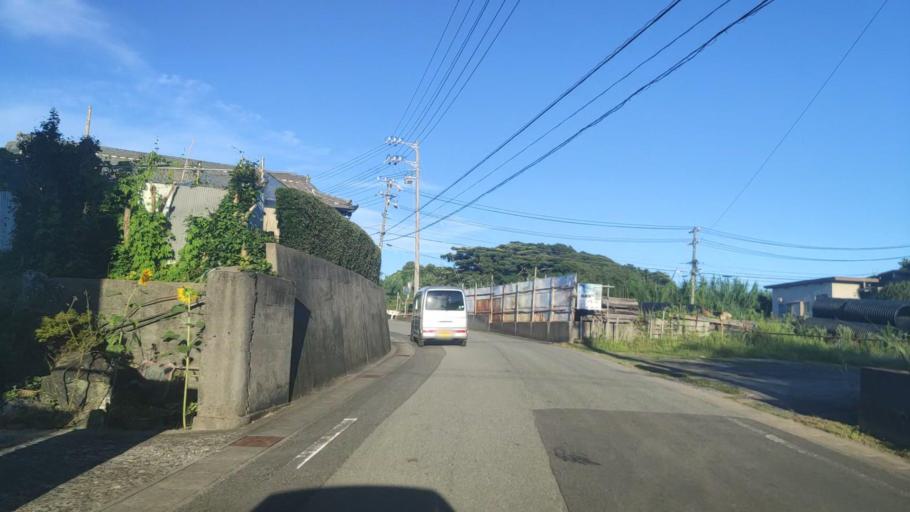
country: JP
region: Mie
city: Toba
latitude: 34.2551
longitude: 136.8332
